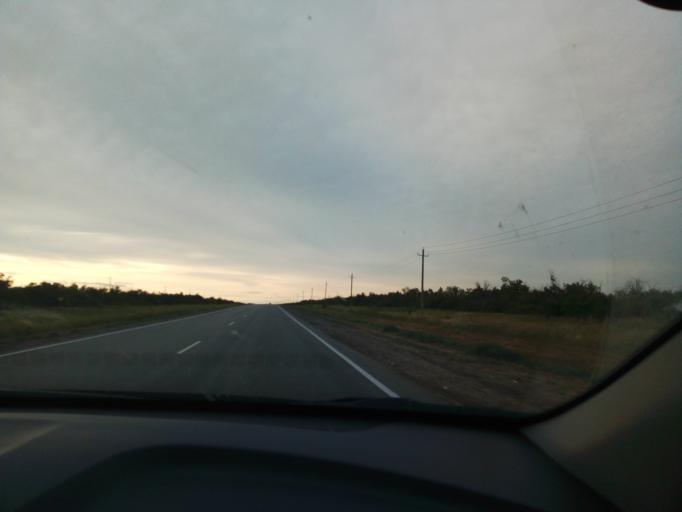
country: RU
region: Volgograd
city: Primorsk
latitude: 49.2794
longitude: 44.8718
